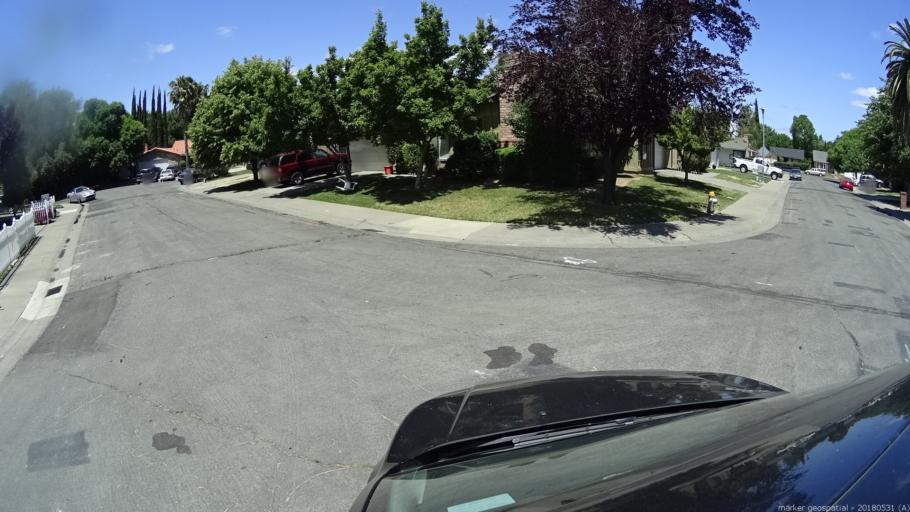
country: US
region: California
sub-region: Sacramento County
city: Sacramento
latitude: 38.6190
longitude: -121.5125
